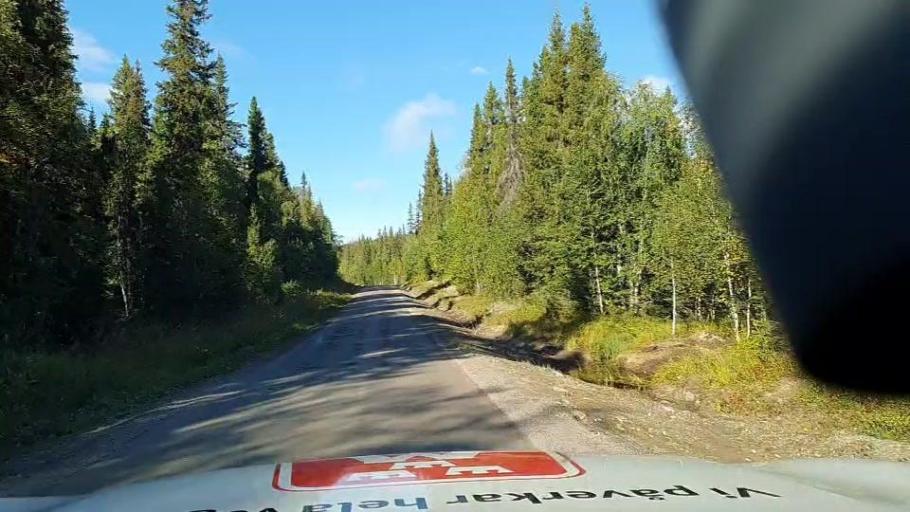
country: SE
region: Jaemtland
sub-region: Stroemsunds Kommun
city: Stroemsund
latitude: 64.5572
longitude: 15.0936
